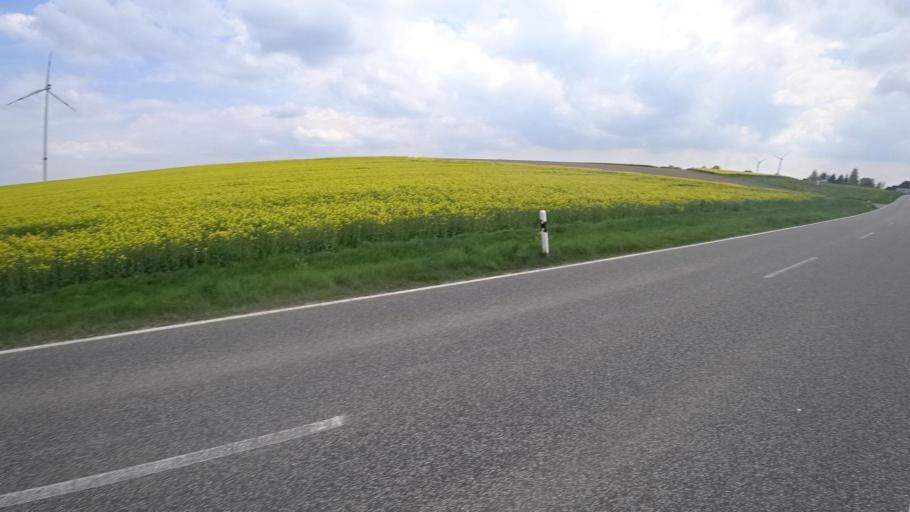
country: DE
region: Rheinland-Pfalz
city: Laubach
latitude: 50.0587
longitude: 7.5133
